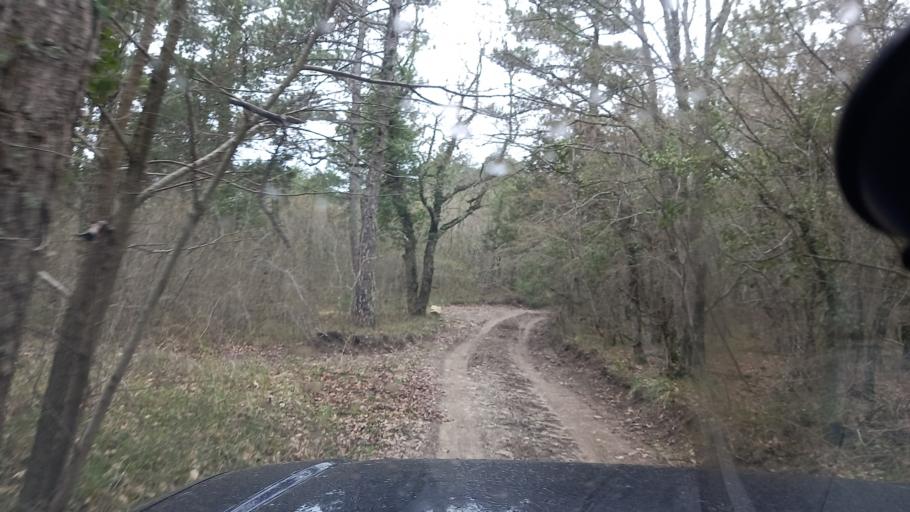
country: RU
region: Krasnodarskiy
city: Arkhipo-Osipovka
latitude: 44.3760
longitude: 38.4731
